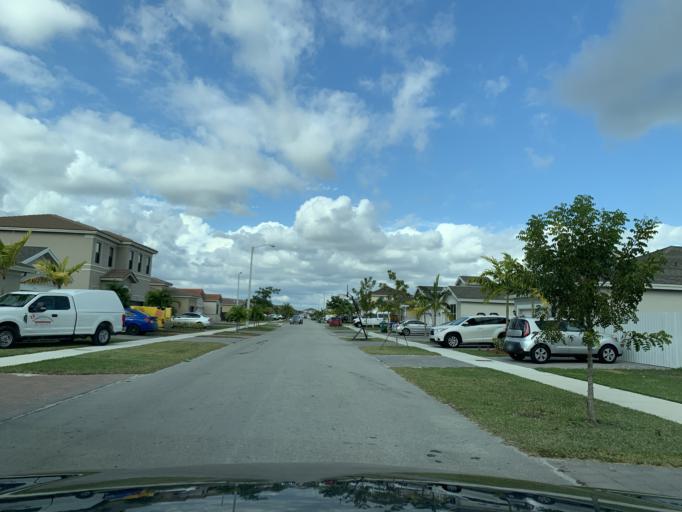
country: US
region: Florida
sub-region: Miami-Dade County
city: Naranja
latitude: 25.5084
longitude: -80.4089
